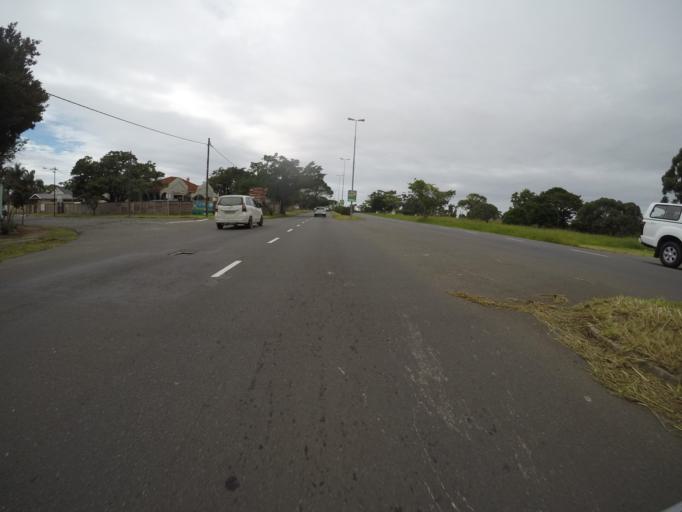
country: ZA
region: Eastern Cape
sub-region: Buffalo City Metropolitan Municipality
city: East London
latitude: -32.9909
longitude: 27.8939
